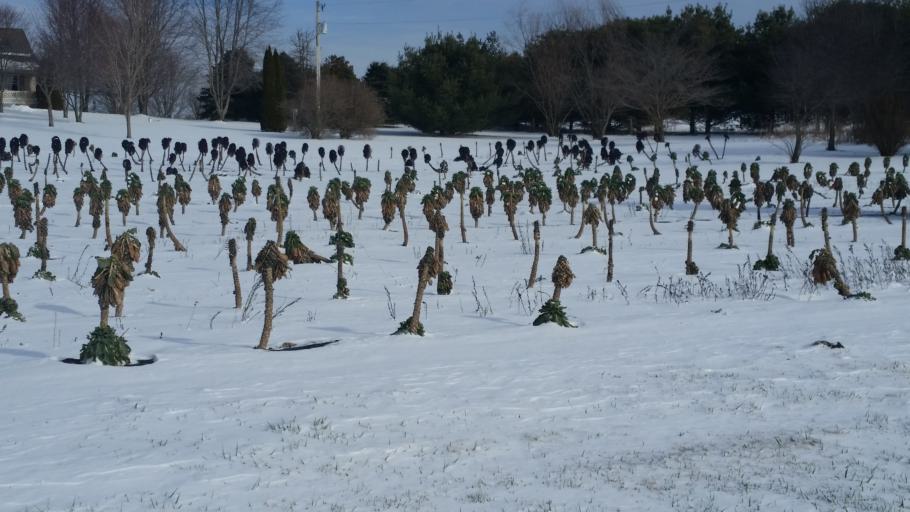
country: US
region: Ohio
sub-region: Knox County
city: Fredericktown
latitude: 40.5193
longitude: -82.6209
